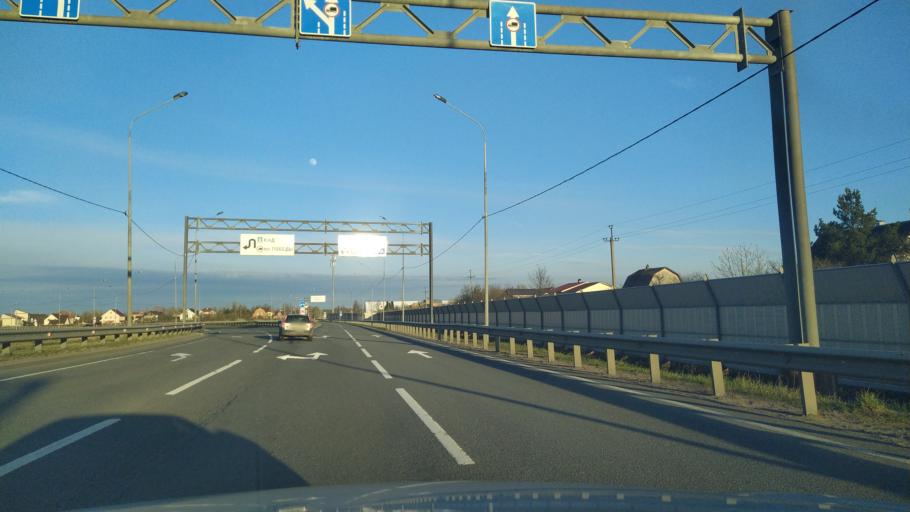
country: RU
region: St.-Petersburg
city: Aleksandrovskaya
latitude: 59.7409
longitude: 30.3196
